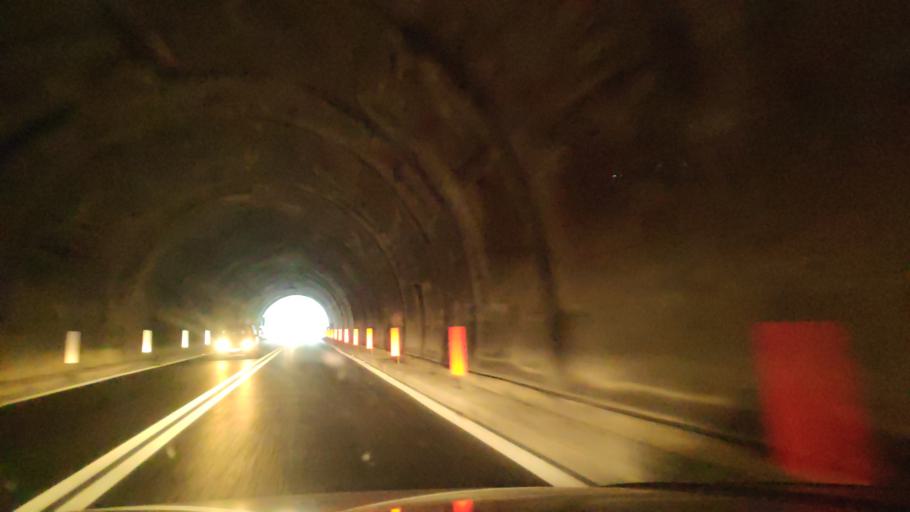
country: IT
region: Calabria
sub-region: Provincia di Reggio Calabria
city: Amato
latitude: 38.4092
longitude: 16.1451
